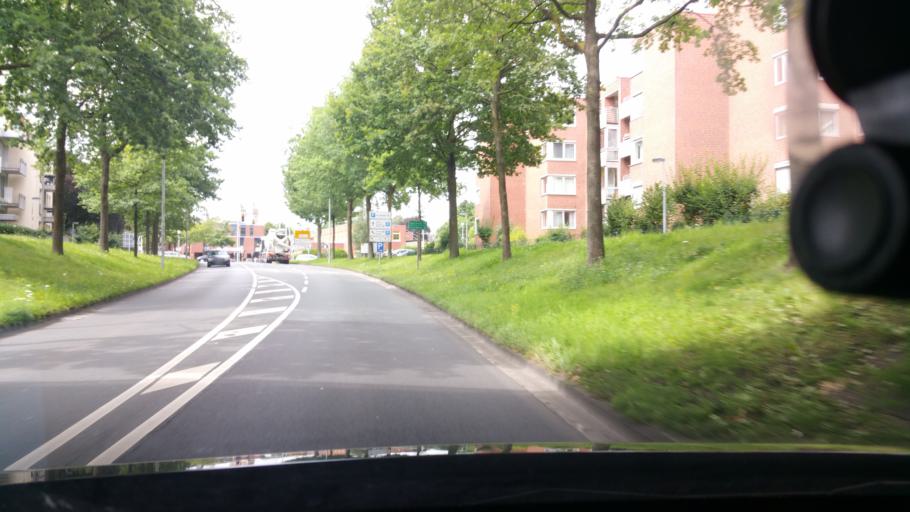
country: DE
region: North Rhine-Westphalia
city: Emsdetten
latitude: 52.1783
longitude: 7.5304
